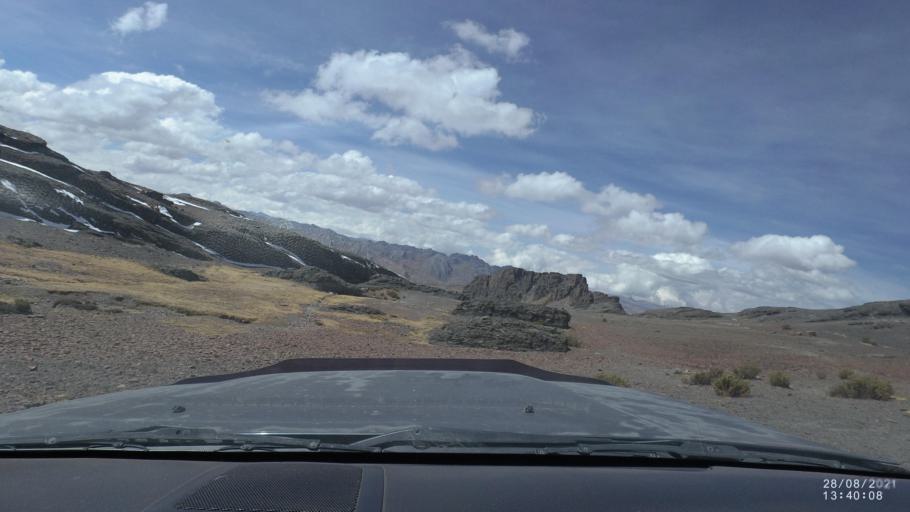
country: BO
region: Cochabamba
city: Sipe Sipe
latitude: -17.2825
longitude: -66.3855
